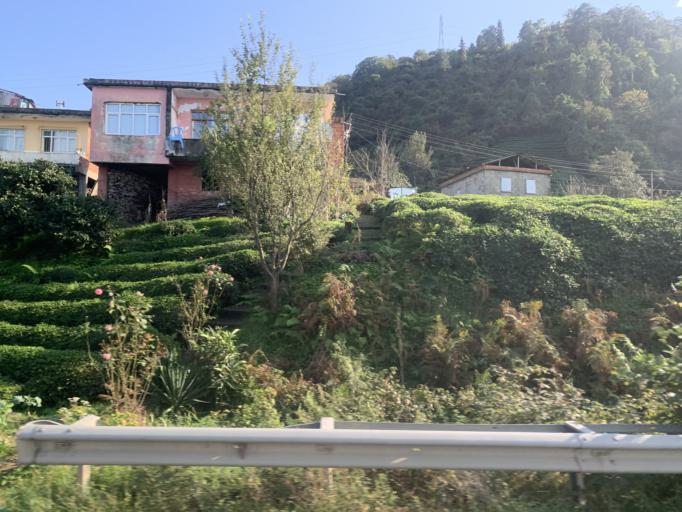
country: TR
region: Trabzon
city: Of
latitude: 40.9368
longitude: 40.2506
